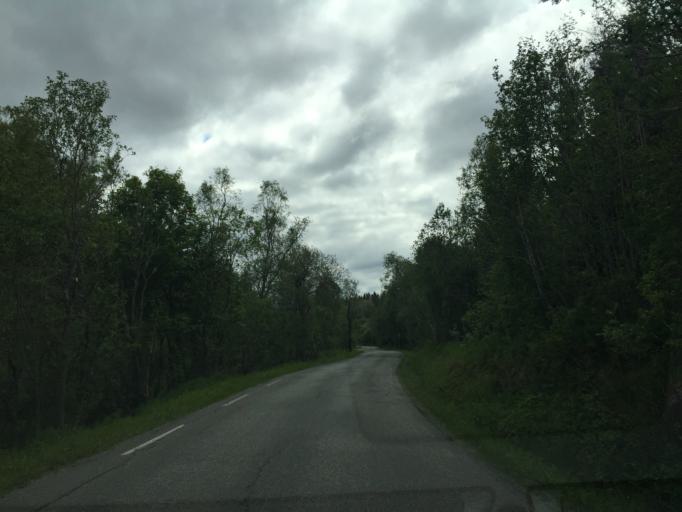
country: NO
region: Nordland
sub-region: Bodo
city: Loding
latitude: 67.3105
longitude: 14.6406
